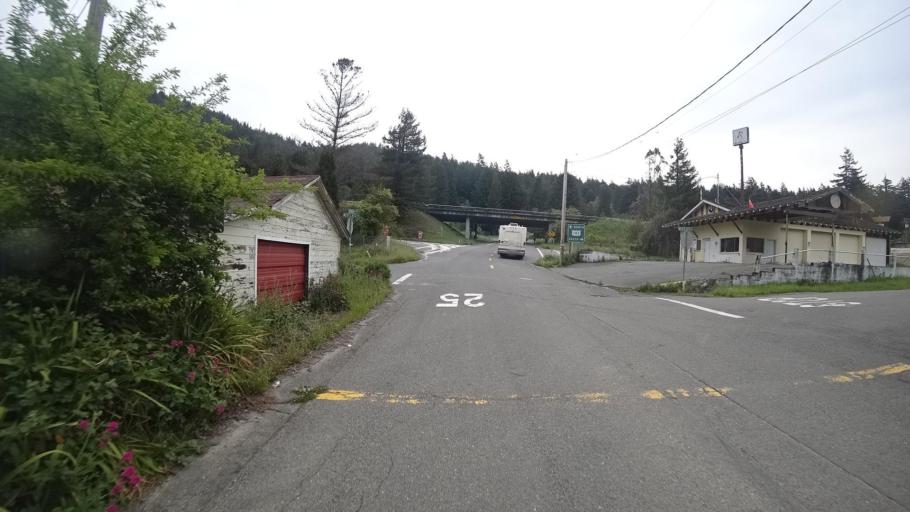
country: US
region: California
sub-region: Humboldt County
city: Redway
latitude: 40.3217
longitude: -123.9223
